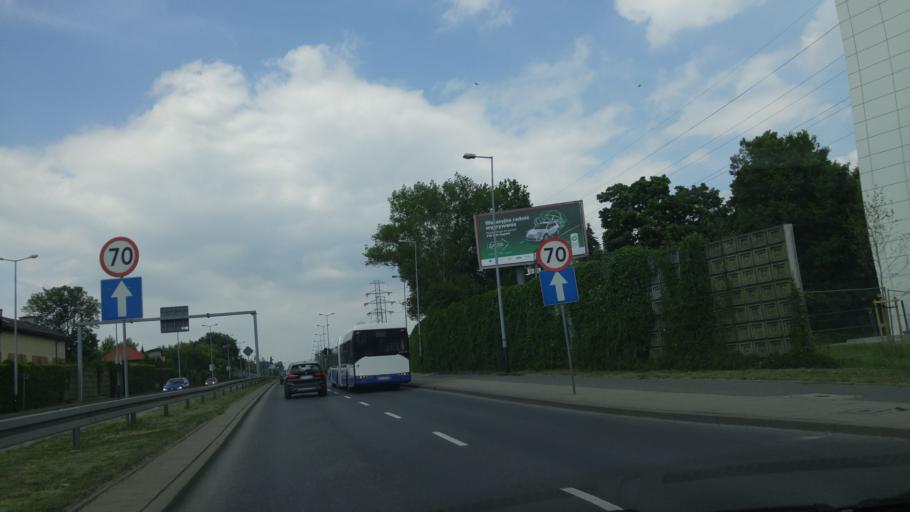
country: PL
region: Lesser Poland Voivodeship
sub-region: Krakow
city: Krakow
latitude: 50.0151
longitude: 19.9454
